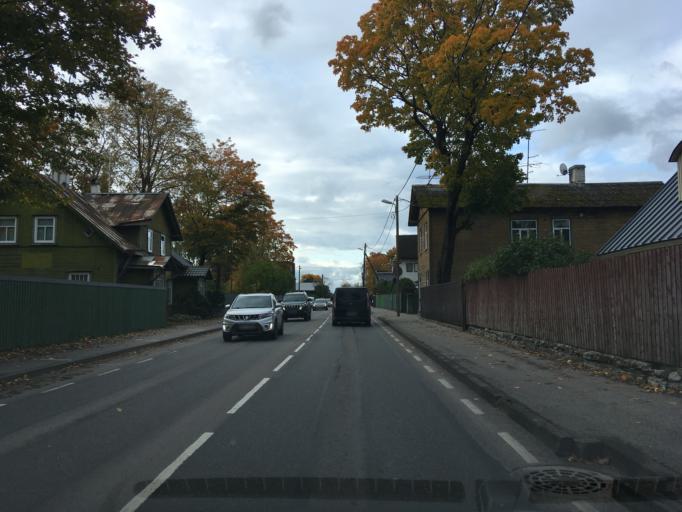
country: EE
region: Harju
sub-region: Saue vald
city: Laagri
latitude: 59.3856
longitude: 24.6758
